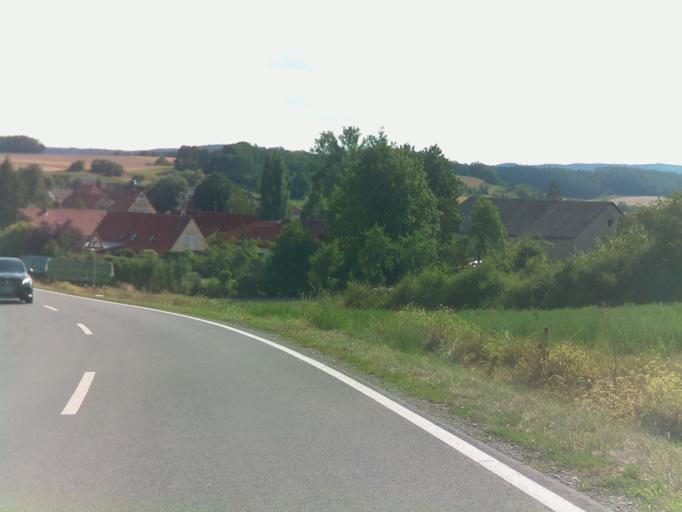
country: DE
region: Bavaria
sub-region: Regierungsbezirk Unterfranken
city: Trappstadt
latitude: 50.2692
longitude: 10.5414
